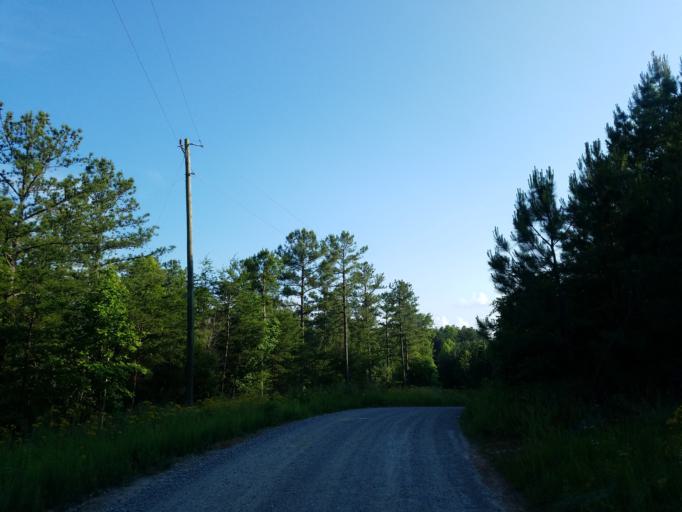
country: US
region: Georgia
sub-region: Pickens County
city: Nelson
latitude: 34.3622
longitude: -84.3256
